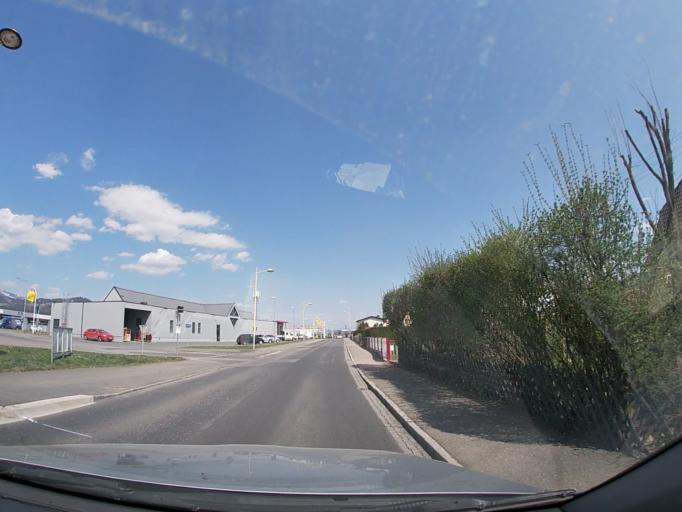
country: AT
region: Styria
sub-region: Politischer Bezirk Murtal
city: Zeltweg
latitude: 47.1965
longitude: 14.7645
